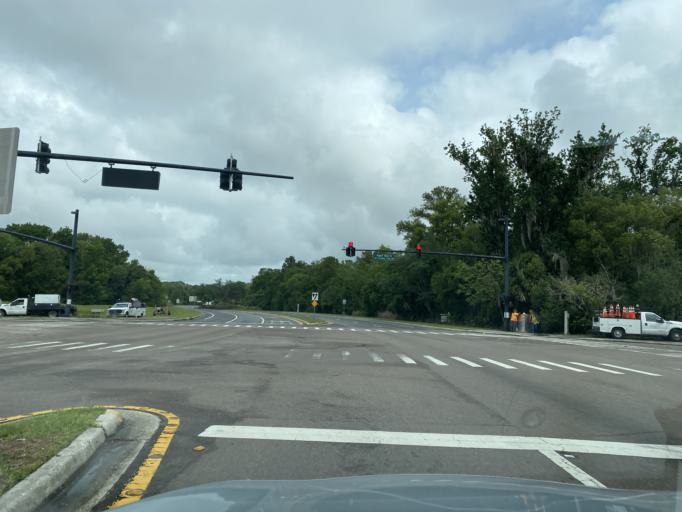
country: US
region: Florida
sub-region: Seminole County
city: Sanford
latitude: 28.7891
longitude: -81.2984
